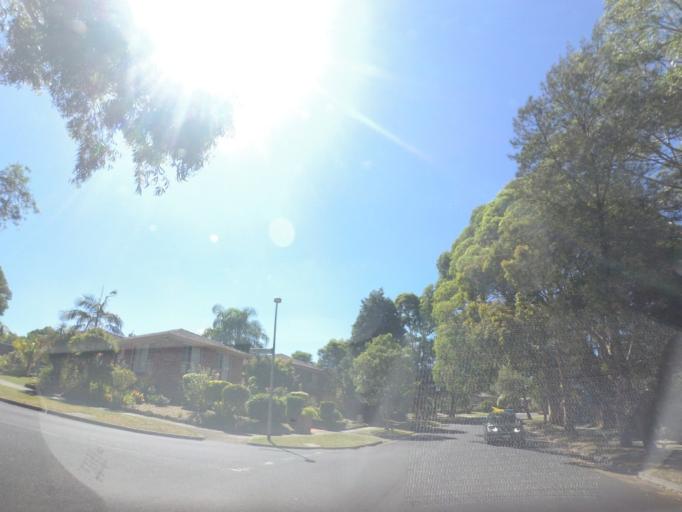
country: AU
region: Victoria
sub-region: Manningham
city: Park Orchards
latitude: -37.7935
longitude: 145.2245
